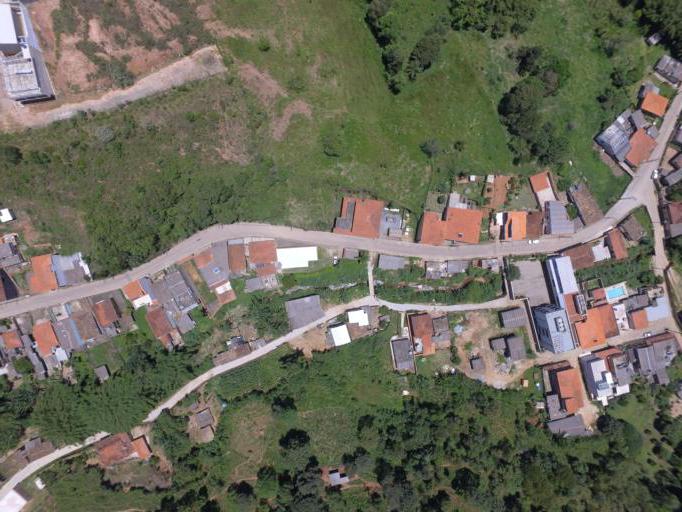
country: BR
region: Minas Gerais
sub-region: Tiradentes
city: Tiradentes
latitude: -21.0631
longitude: -44.0810
